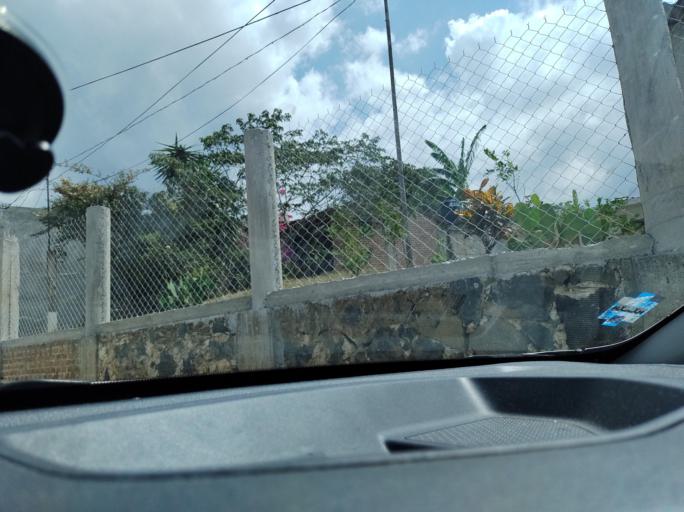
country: MX
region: Veracruz
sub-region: Coatepec
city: Bella Esperanza
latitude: 19.4339
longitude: -96.8648
